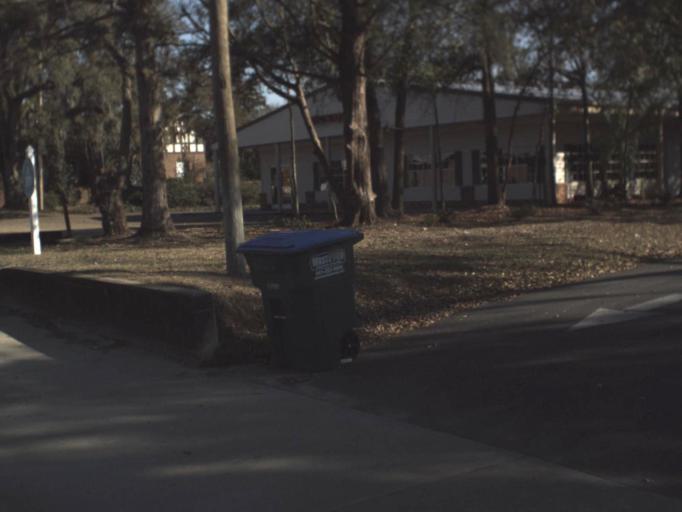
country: US
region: Florida
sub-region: Jackson County
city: Marianna
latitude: 30.7755
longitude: -85.2324
